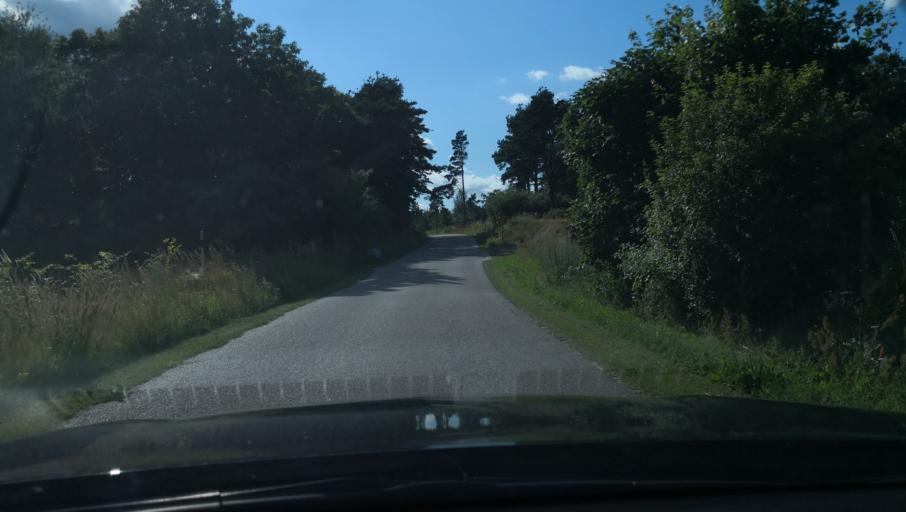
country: SE
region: Skane
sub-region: Simrishamns Kommun
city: Kivik
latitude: 55.7681
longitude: 14.1915
